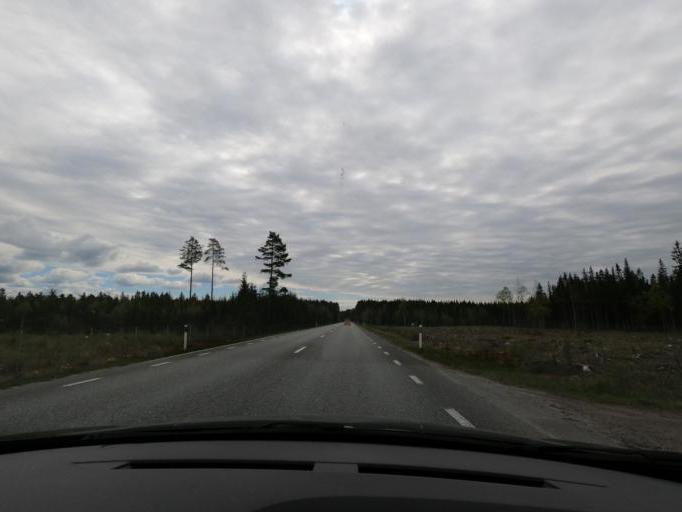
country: SE
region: Vaestra Goetaland
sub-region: Tranemo Kommun
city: Langhem
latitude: 57.5783
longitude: 13.2235
